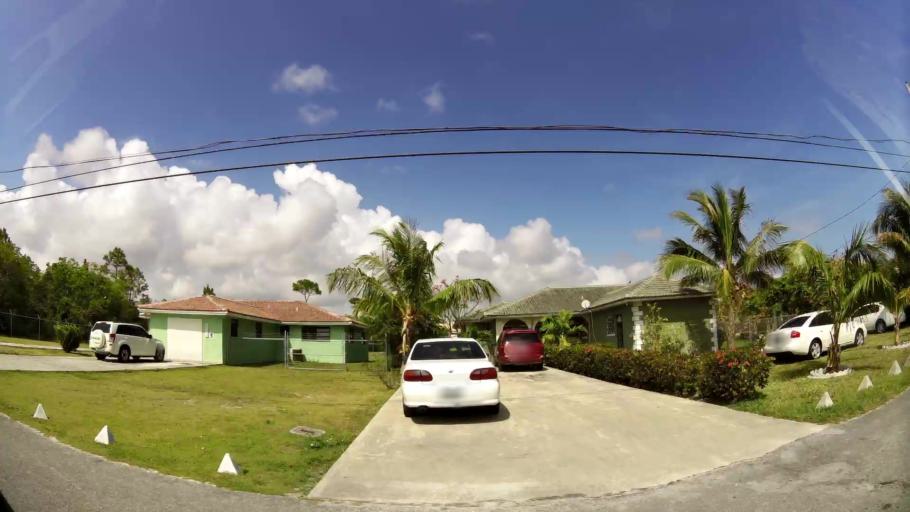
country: BS
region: Freeport
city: Freeport
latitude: 26.5021
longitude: -78.7049
